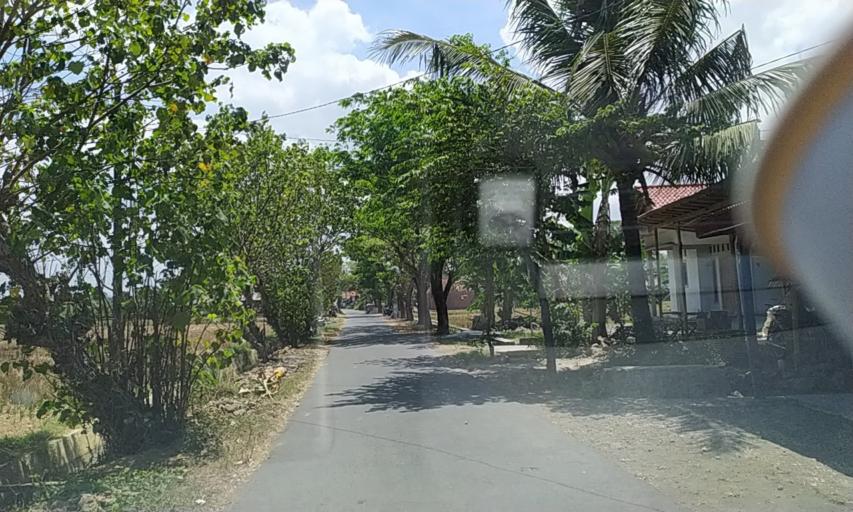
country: ID
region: Central Java
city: Mernek
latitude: -7.6178
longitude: 109.1859
